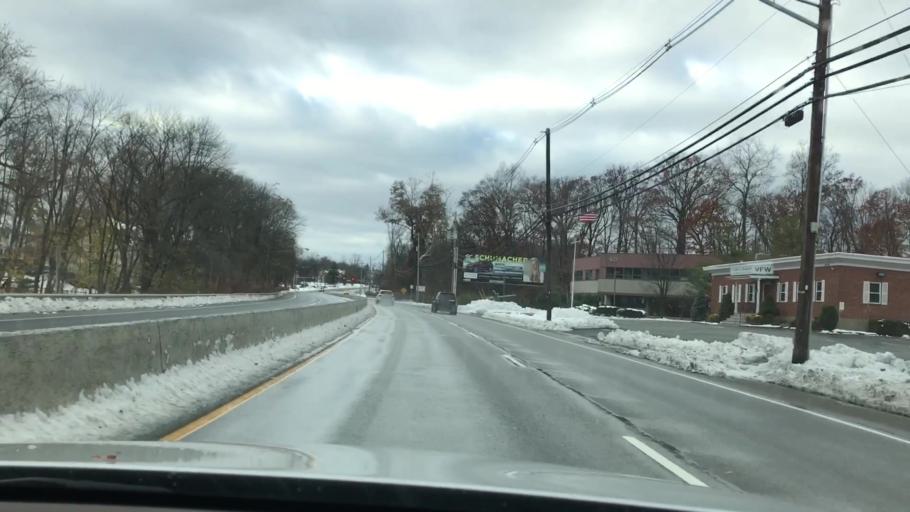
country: US
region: New Jersey
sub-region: Morris County
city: Parsippany
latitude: 40.8258
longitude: -74.4211
